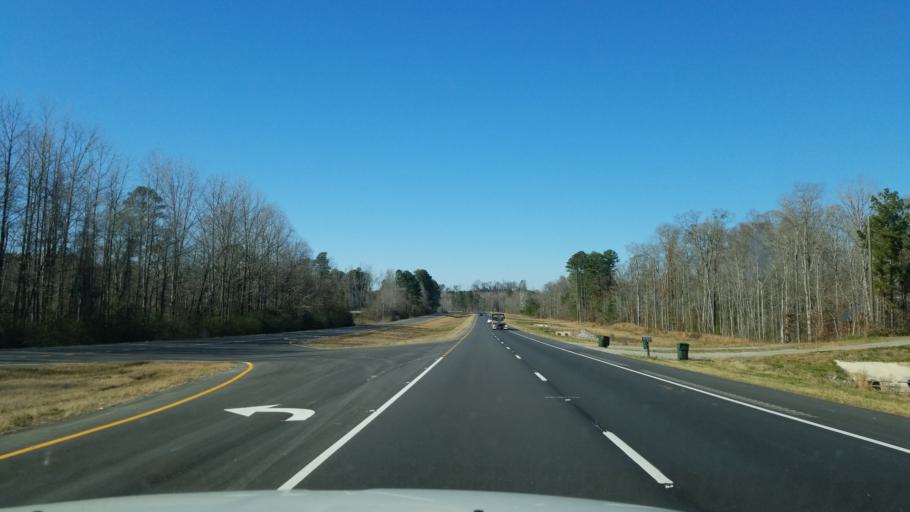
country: US
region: Alabama
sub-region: Pickens County
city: Reform
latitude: 33.3667
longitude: -87.9826
